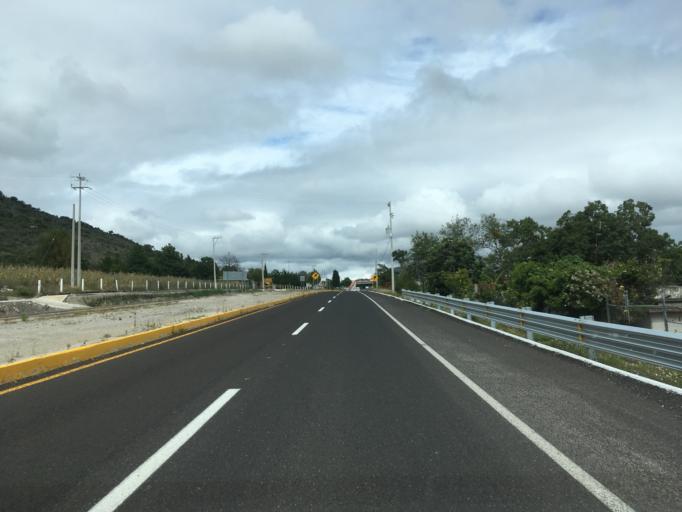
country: MX
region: Hidalgo
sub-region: Atotonilco el Grande
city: Santa Maria Amajac
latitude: 20.3602
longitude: -98.7197
